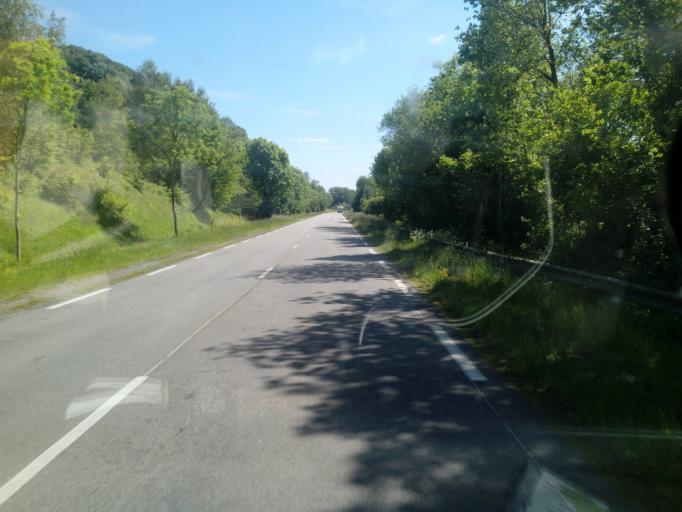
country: FR
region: Haute-Normandie
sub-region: Departement de la Seine-Maritime
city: Tancarville
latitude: 49.4252
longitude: 0.4247
